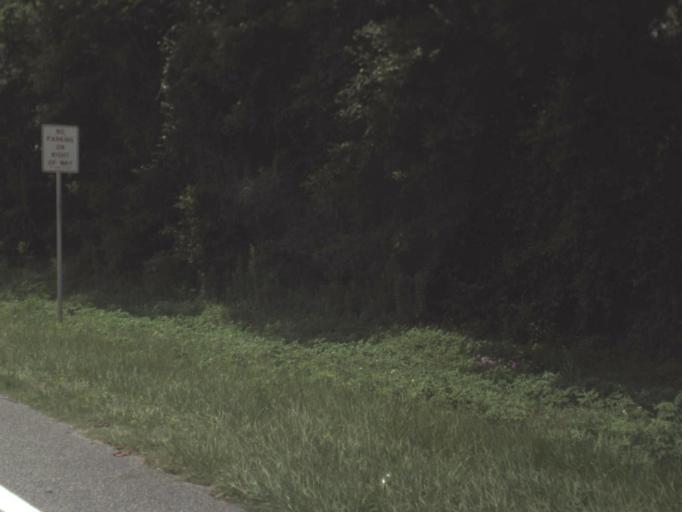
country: US
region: Florida
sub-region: Columbia County
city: Watertown
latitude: 30.1807
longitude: -82.5957
